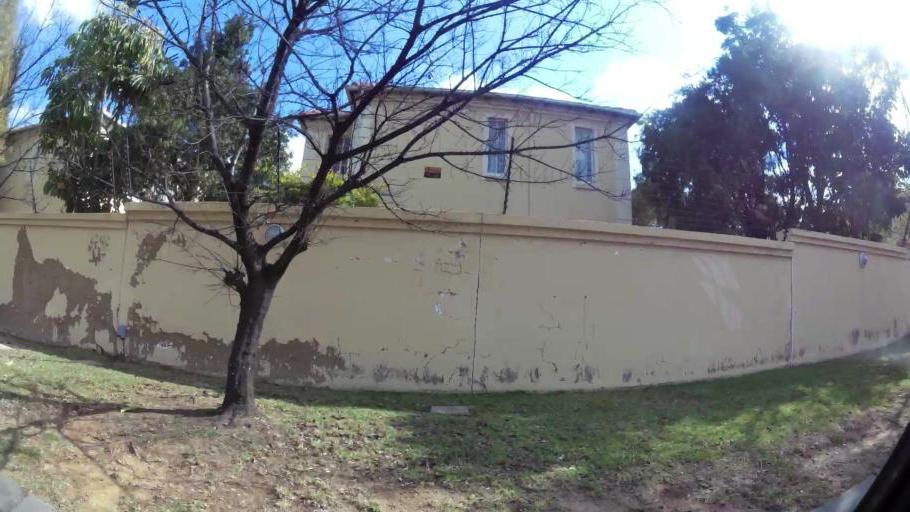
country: ZA
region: Gauteng
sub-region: West Rand District Municipality
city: Muldersdriseloop
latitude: -26.0592
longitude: 27.9662
